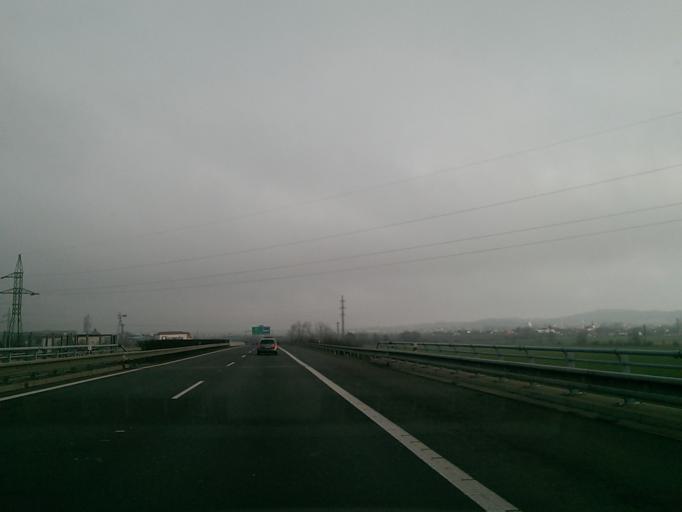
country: CZ
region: Olomoucky
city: Grygov
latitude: 49.5564
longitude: 17.2959
